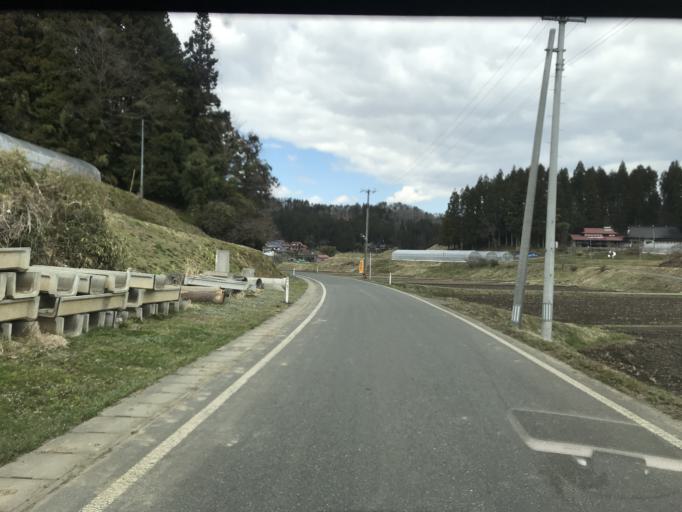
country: JP
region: Iwate
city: Ichinoseki
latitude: 38.9577
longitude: 141.0895
